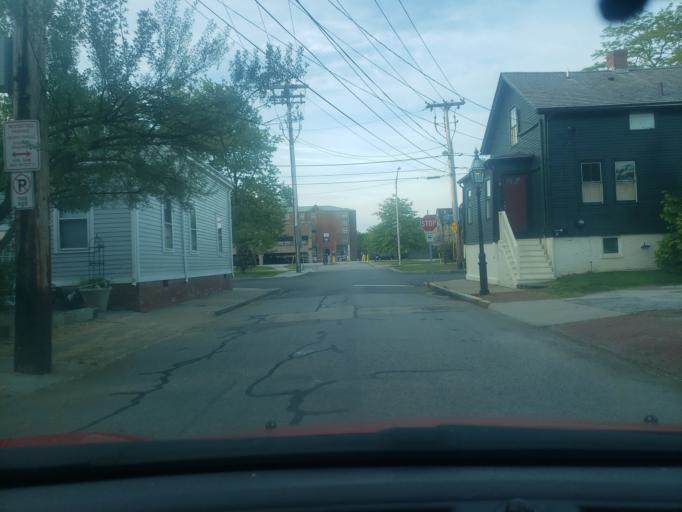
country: US
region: Rhode Island
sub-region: Newport County
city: Newport
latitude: 41.4917
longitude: -71.3195
